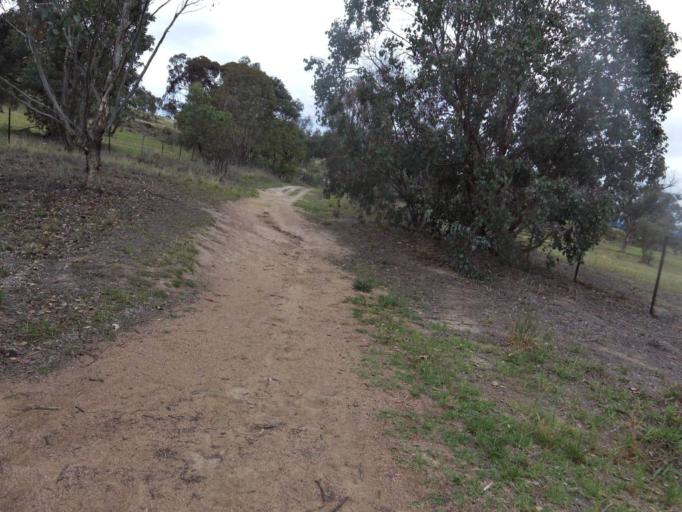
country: AU
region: Australian Capital Territory
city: Macquarie
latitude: -35.3496
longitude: 149.0237
